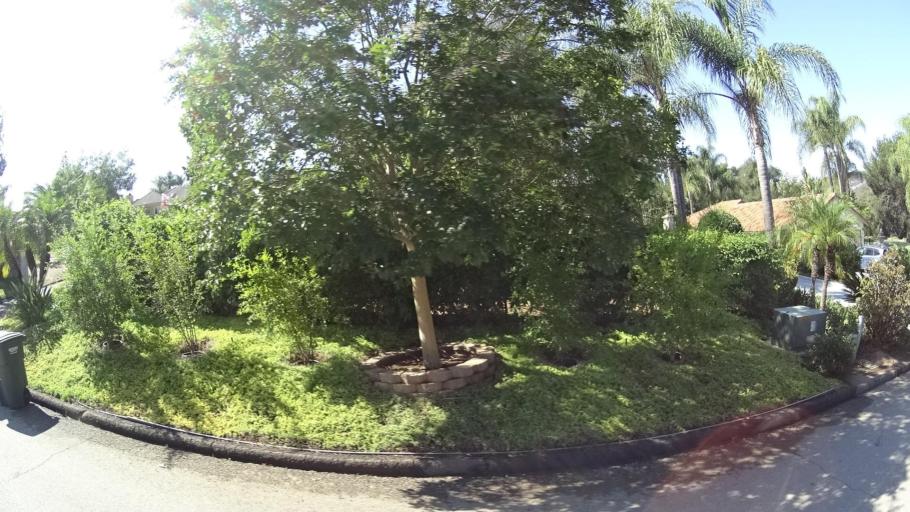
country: US
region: California
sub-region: San Diego County
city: Escondido
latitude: 33.0884
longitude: -117.1066
